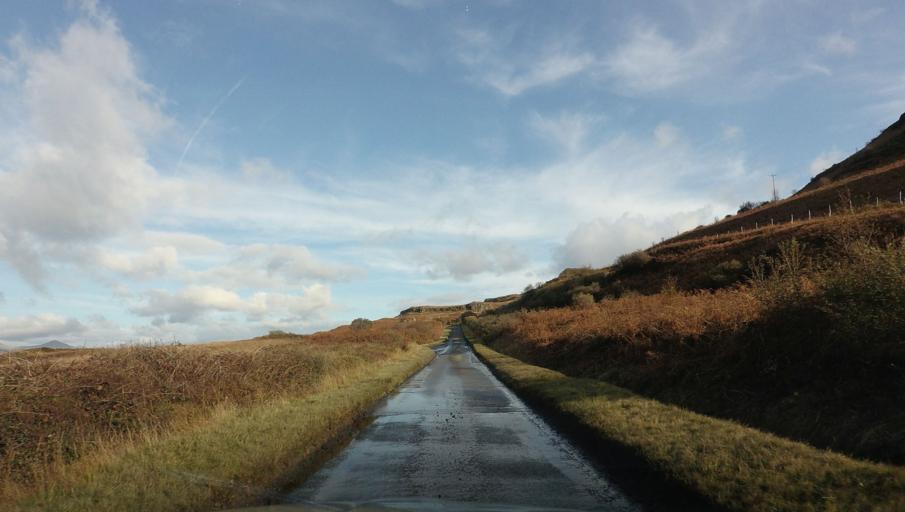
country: GB
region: Scotland
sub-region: Argyll and Bute
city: Isle Of Mull
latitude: 56.3399
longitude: -6.1349
